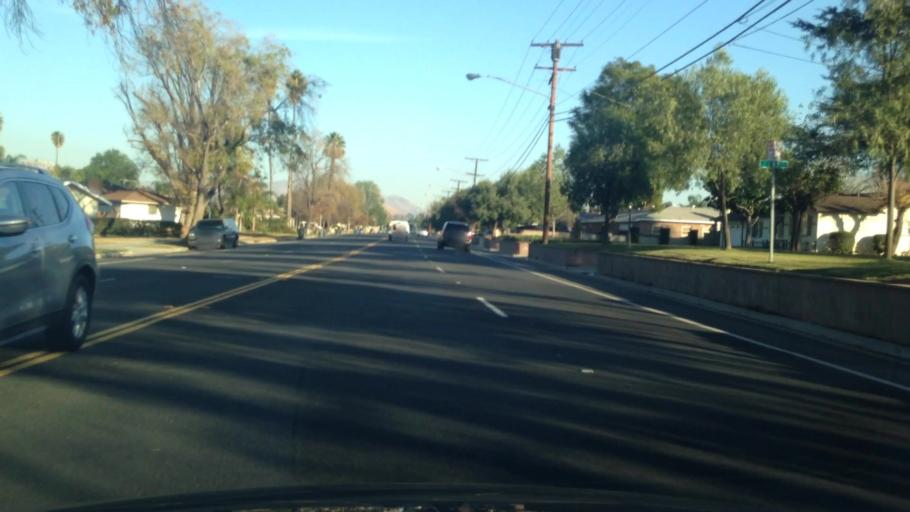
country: US
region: California
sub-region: Riverside County
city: Riverside
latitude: 33.9624
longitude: -117.4250
